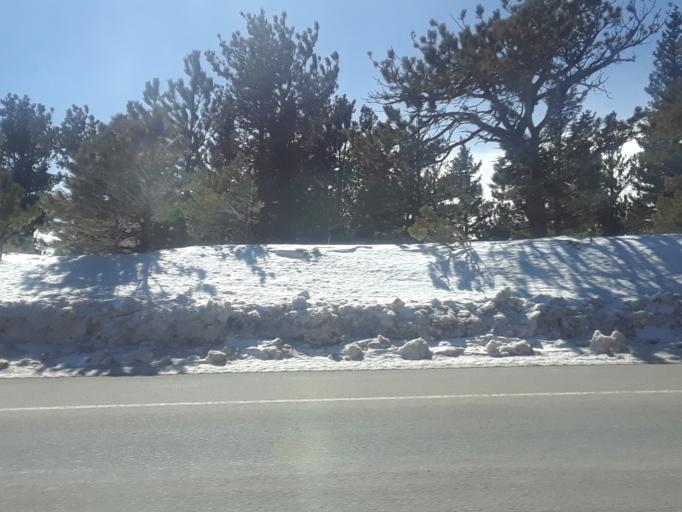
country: US
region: Colorado
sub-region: Boulder County
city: Nederland
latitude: 40.0131
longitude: -105.5075
